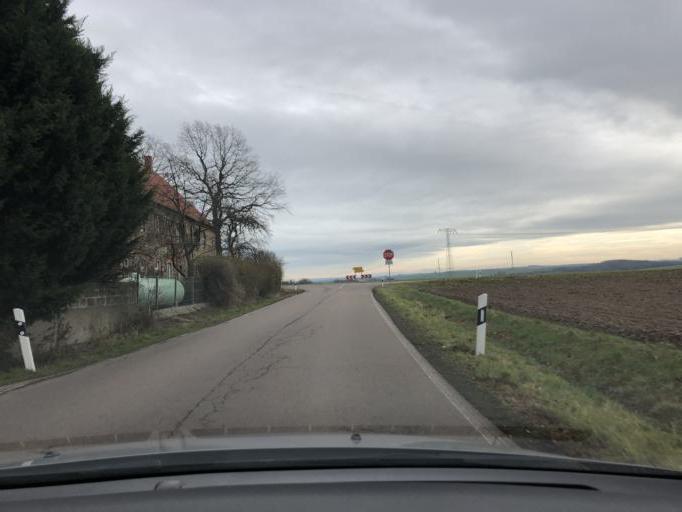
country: DE
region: Saxony
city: Nossen
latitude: 51.0685
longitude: 13.3215
